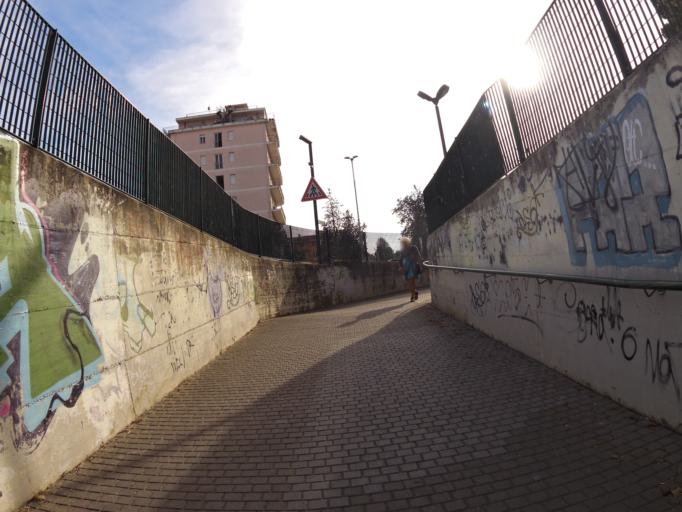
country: IT
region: The Marches
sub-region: Provincia di Macerata
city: Porto Recanati
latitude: 43.4262
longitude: 13.6636
